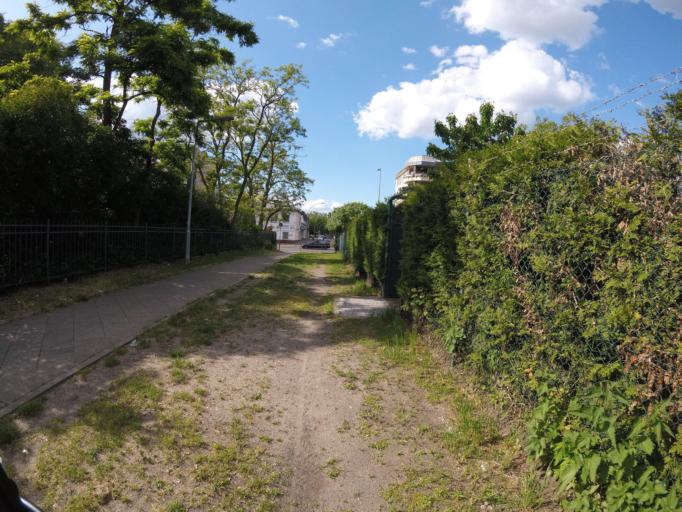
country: DE
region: Berlin
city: Wilhelmstadt
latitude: 52.5260
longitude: 13.1820
